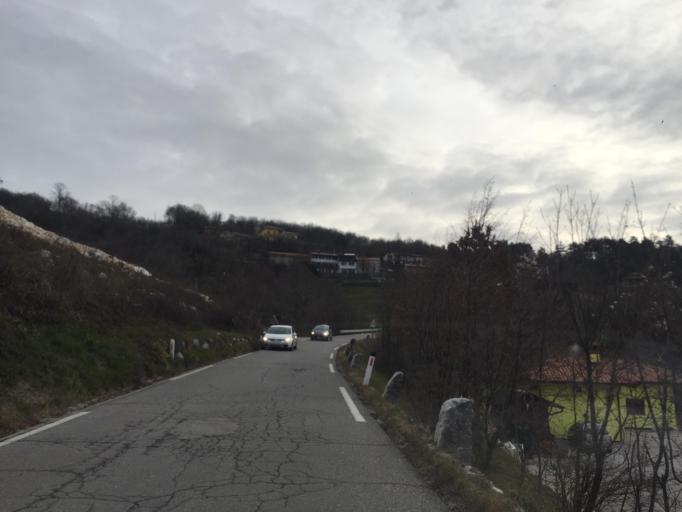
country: SI
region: Nova Gorica
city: Kromberk
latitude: 45.9845
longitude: 13.7098
